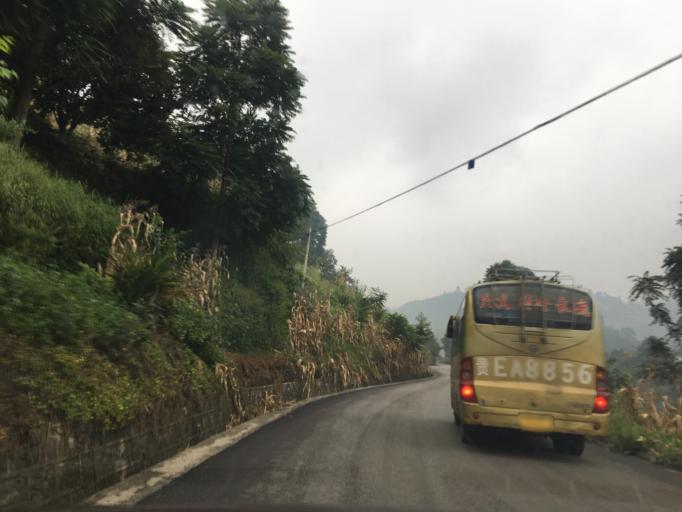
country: CN
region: Guizhou Sheng
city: Liupanshui
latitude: 26.0654
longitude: 105.1402
